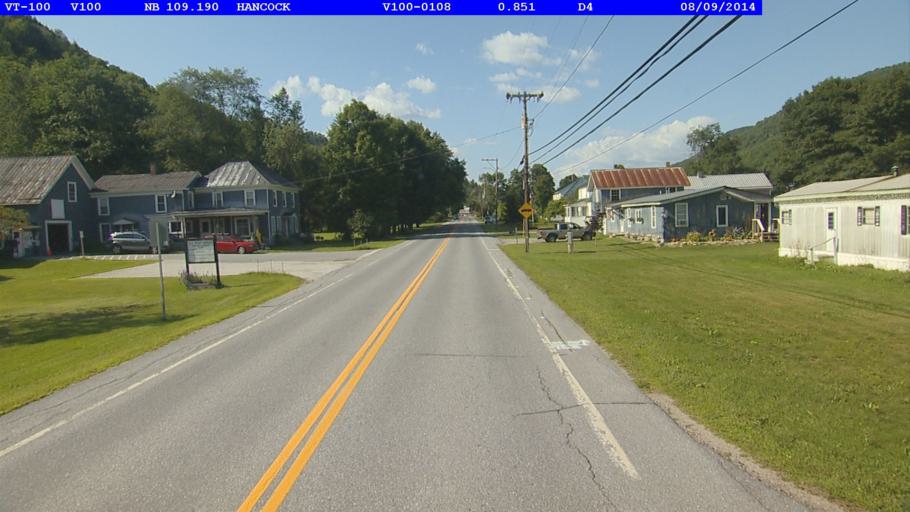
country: US
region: Vermont
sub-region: Orange County
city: Randolph
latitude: 43.9211
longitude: -72.8401
